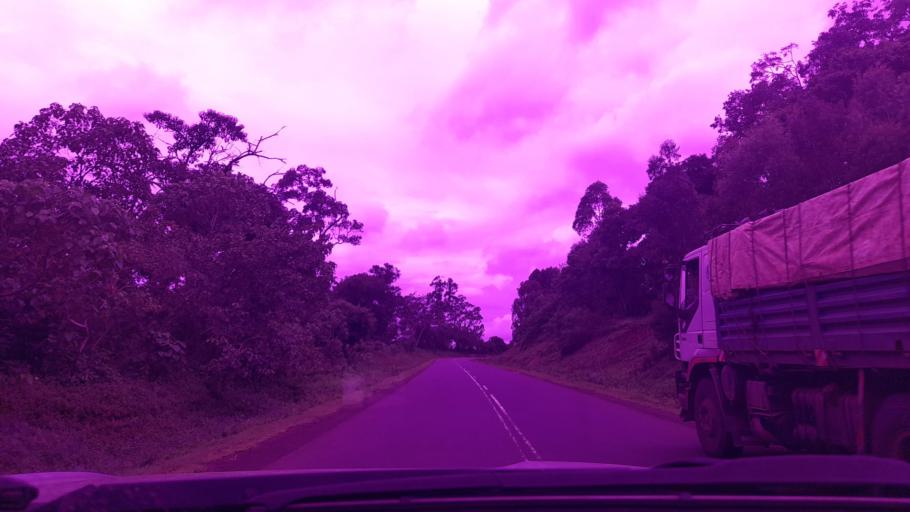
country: ET
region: Southern Nations, Nationalities, and People's Region
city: Bonga
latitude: 7.2803
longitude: 35.9439
